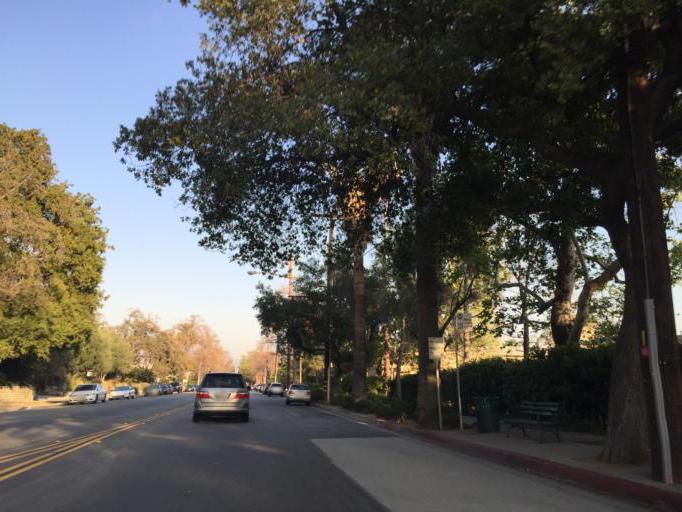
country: US
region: California
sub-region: Los Angeles County
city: Sierra Madre
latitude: 34.1618
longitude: -118.0675
